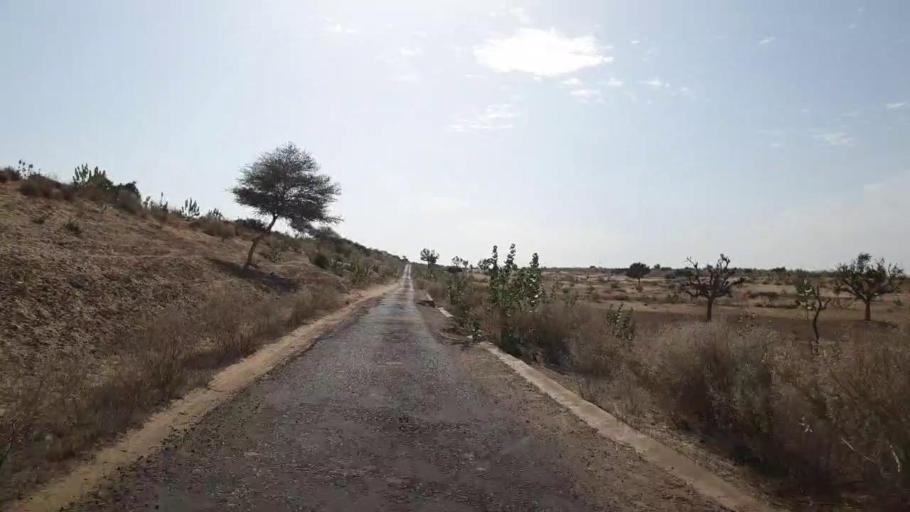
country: PK
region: Sindh
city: Nabisar
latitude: 25.0599
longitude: 70.0299
